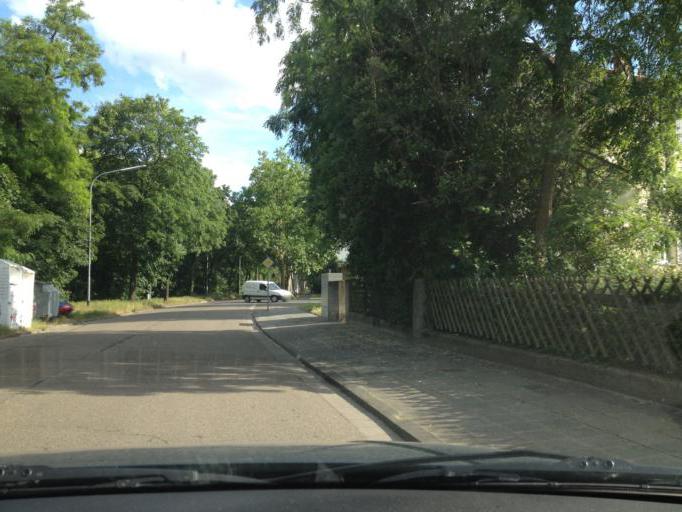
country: DE
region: Rheinland-Pfalz
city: Frankenthal
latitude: 49.5315
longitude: 8.3490
